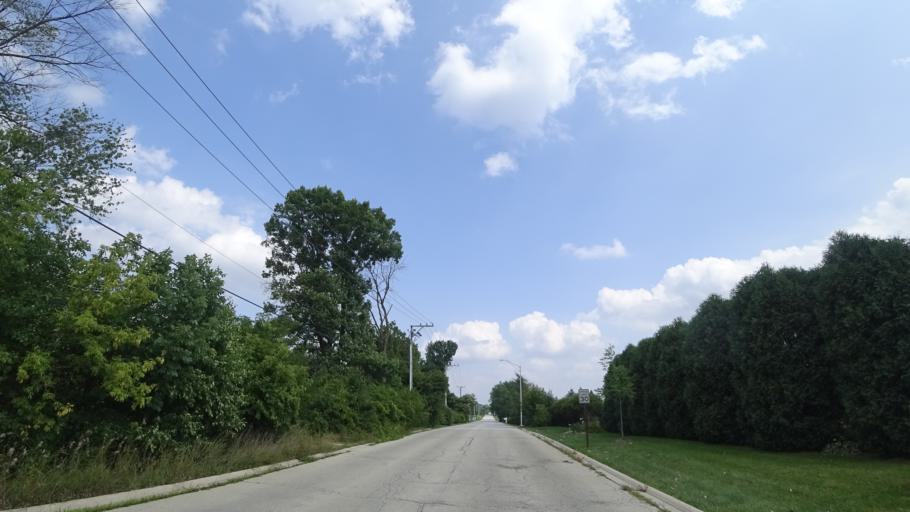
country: US
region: Illinois
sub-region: Will County
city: Goodings Grove
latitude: 41.6368
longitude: -87.9002
